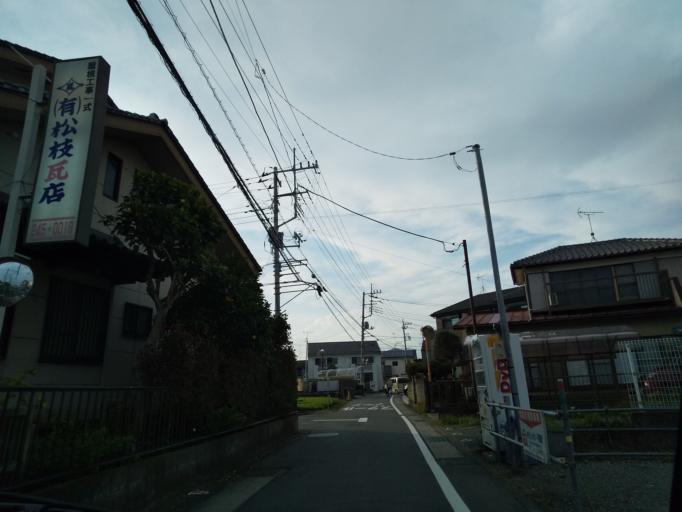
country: JP
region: Kanagawa
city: Zama
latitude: 35.5074
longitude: 139.3616
